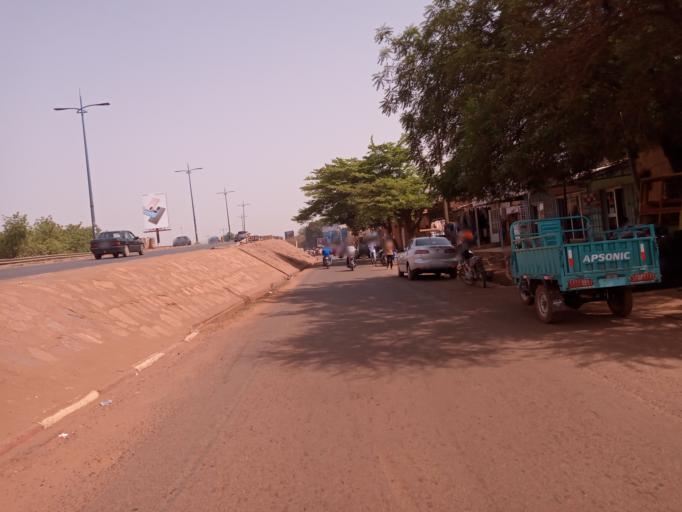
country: ML
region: Bamako
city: Bamako
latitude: 12.6124
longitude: -7.9986
